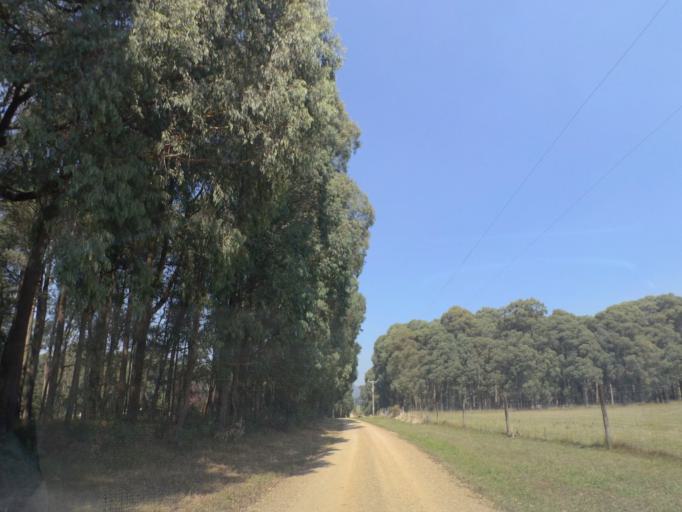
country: AU
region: Victoria
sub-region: Yarra Ranges
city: Healesville
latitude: -37.5617
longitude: 145.6448
